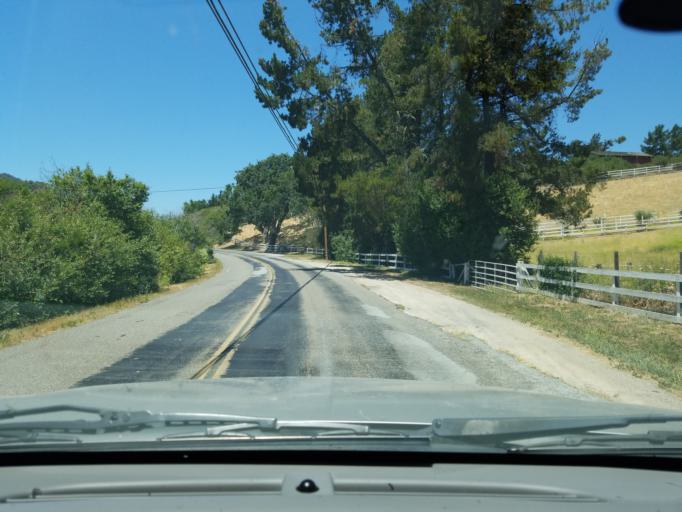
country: US
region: California
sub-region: Monterey County
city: Carmel Valley Village
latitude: 36.4442
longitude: -121.6681
